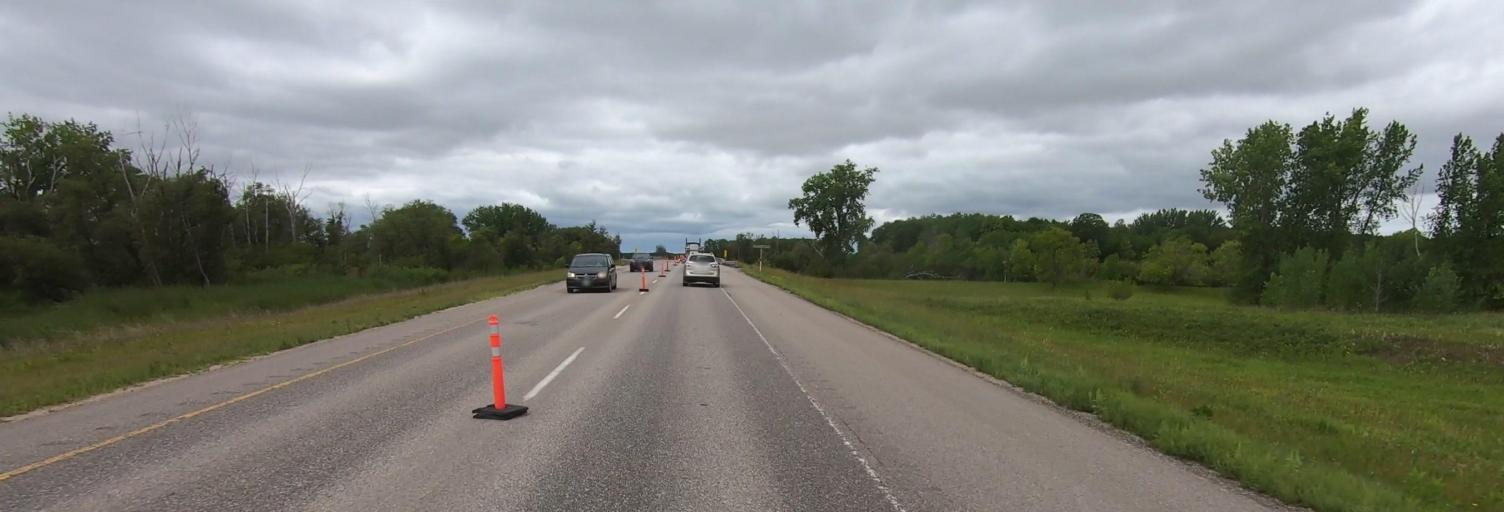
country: CA
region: Manitoba
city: Portage la Prairie
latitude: 49.9707
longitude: -98.0956
